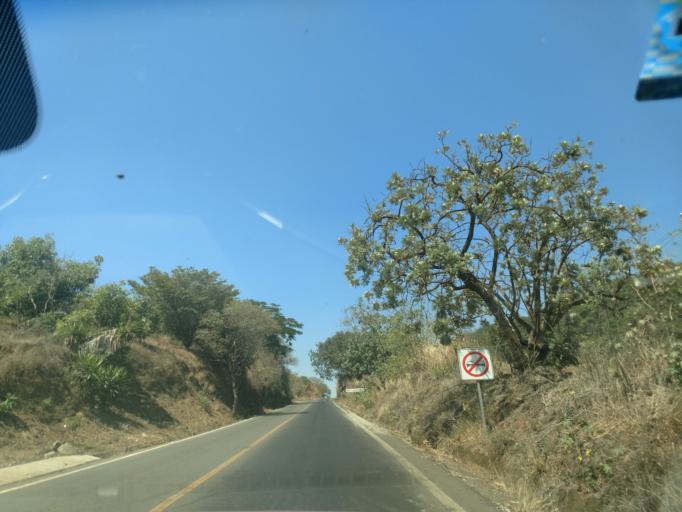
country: MX
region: Nayarit
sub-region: Tepic
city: La Corregidora
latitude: 21.5000
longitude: -104.7731
